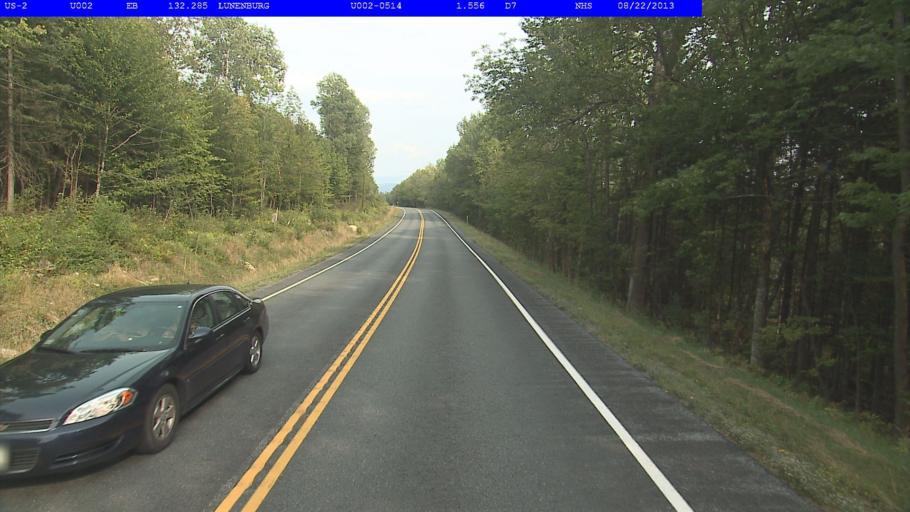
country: US
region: New Hampshire
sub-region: Grafton County
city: Littleton
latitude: 44.4650
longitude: -71.7447
